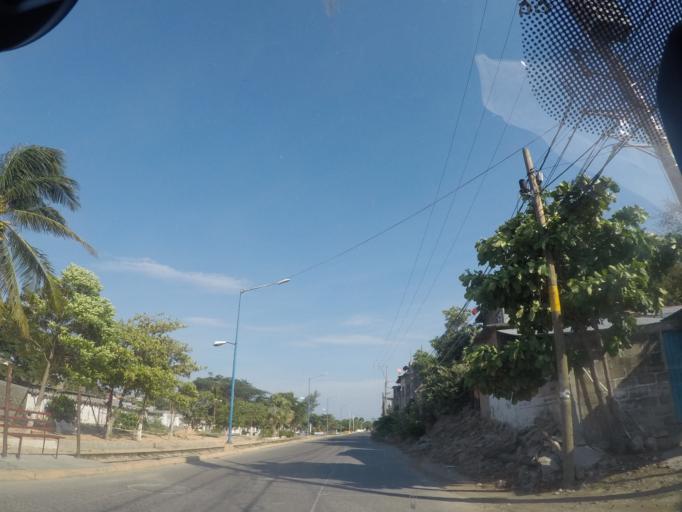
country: MX
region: Oaxaca
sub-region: Salina Cruz
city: Salina Cruz
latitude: 16.1870
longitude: -95.2012
